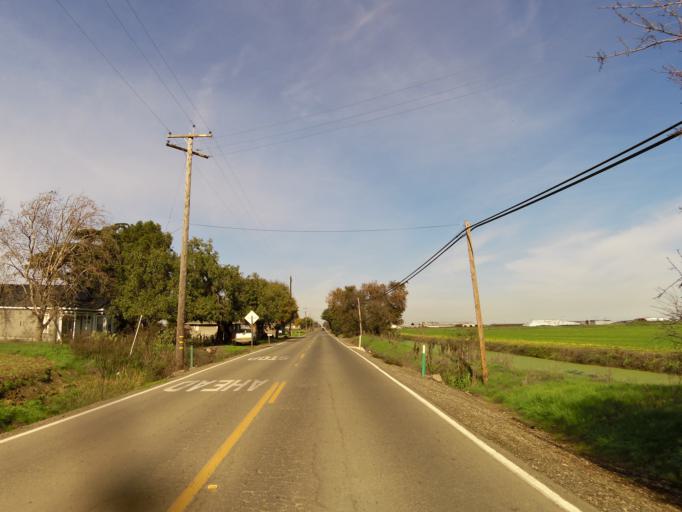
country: US
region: California
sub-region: San Joaquin County
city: Thornton
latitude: 38.3226
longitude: -121.4171
